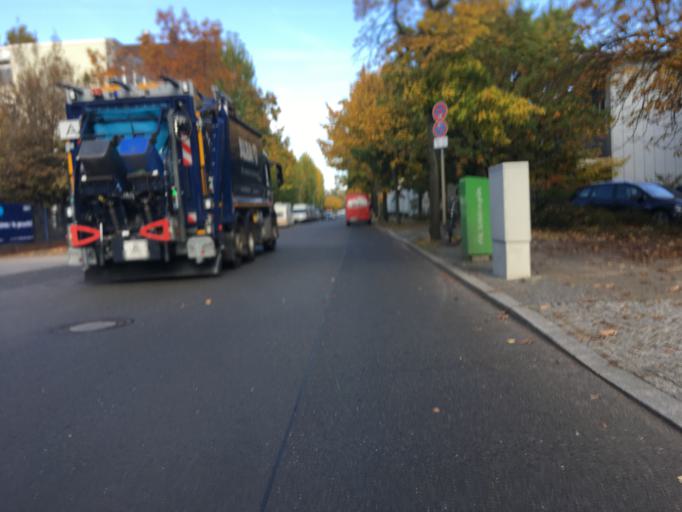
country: DE
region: Berlin
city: Wilhelmsruh
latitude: 52.5795
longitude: 13.3520
